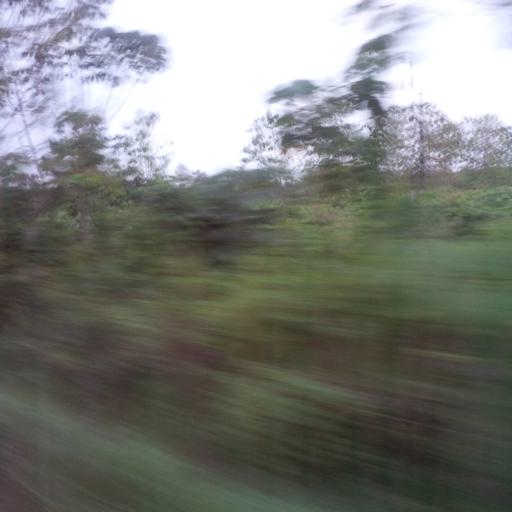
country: EC
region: Canar
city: La Troncal
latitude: -2.3421
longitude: -79.3774
